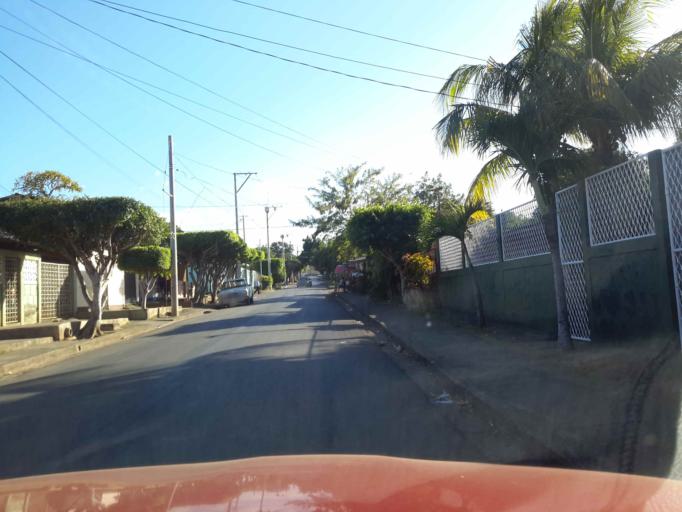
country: NI
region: Managua
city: Managua
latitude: 12.1183
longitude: -86.2938
